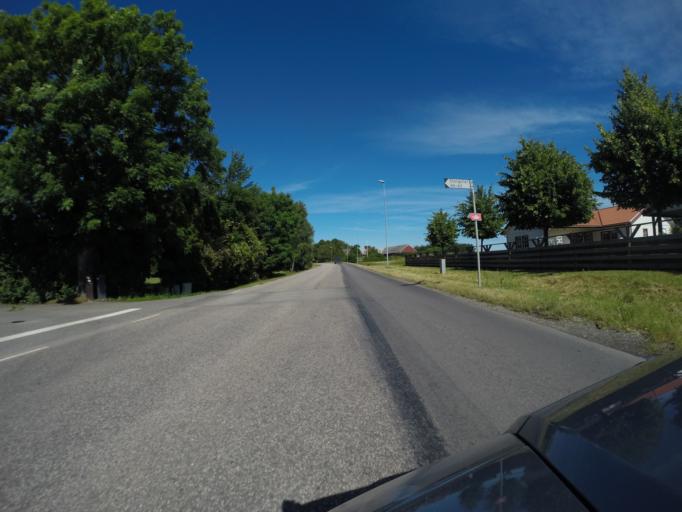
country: SE
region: Skane
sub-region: Bjuvs Kommun
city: Bjuv
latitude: 56.0921
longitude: 12.9057
